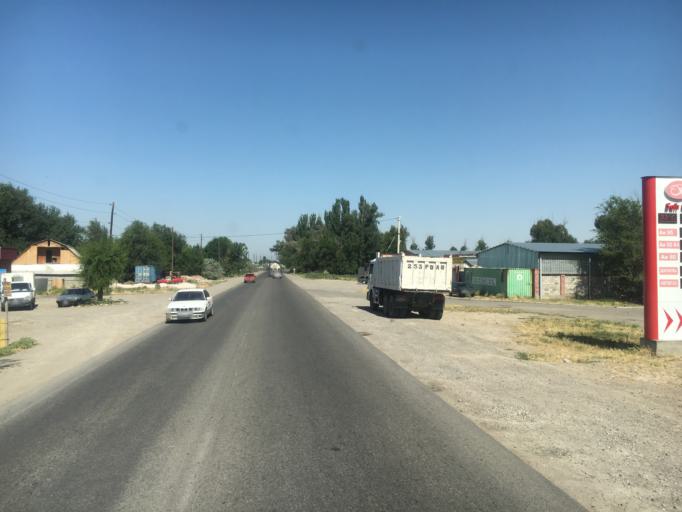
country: KZ
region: Zhambyl
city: Taraz
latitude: 42.9431
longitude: 71.4127
